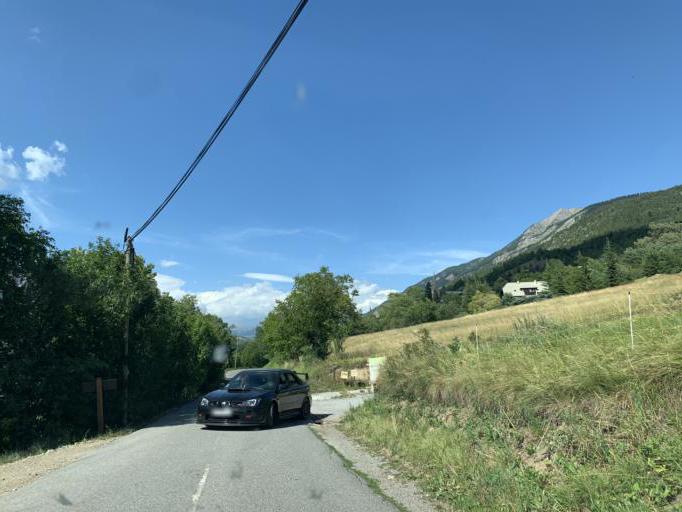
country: FR
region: Provence-Alpes-Cote d'Azur
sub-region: Departement des Hautes-Alpes
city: Embrun
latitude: 44.5843
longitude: 6.5302
